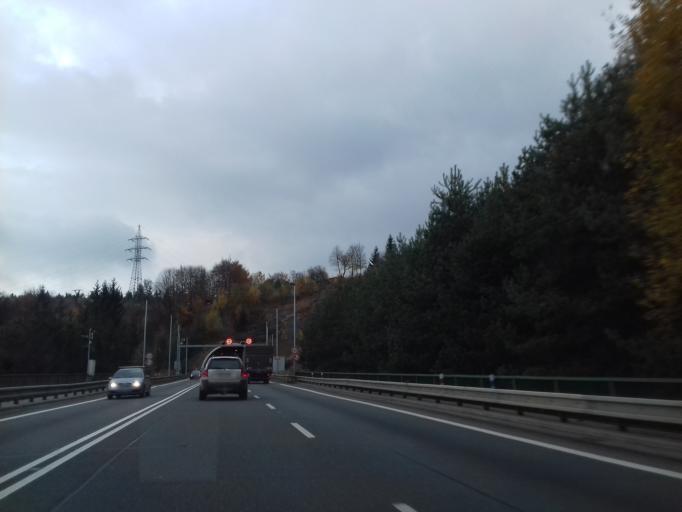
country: CZ
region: Pardubicky
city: Kuncina
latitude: 49.7484
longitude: 16.5816
